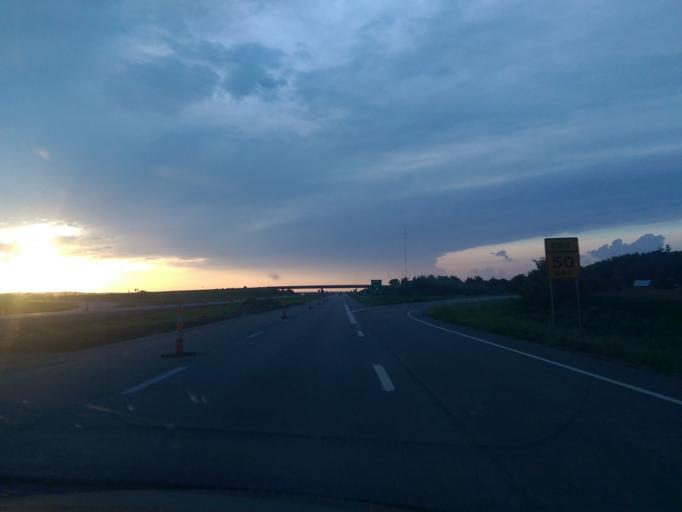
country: US
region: Missouri
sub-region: Atchison County
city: Rock Port
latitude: 40.3658
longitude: -95.5281
